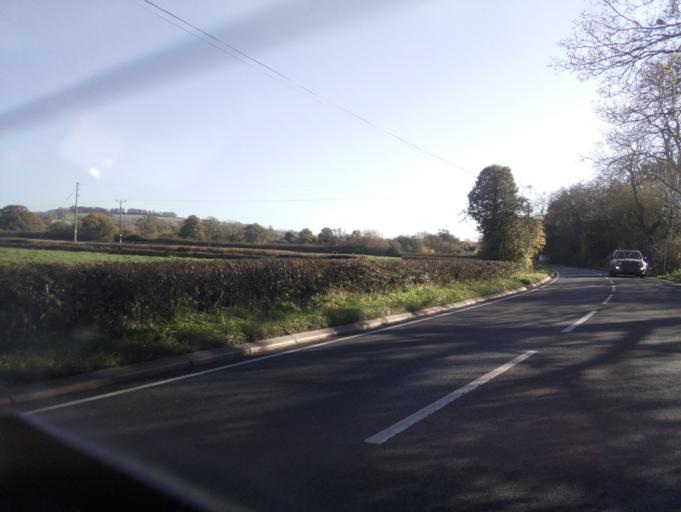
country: GB
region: England
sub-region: Dorset
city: Sherborne
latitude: 50.8679
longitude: -2.4775
